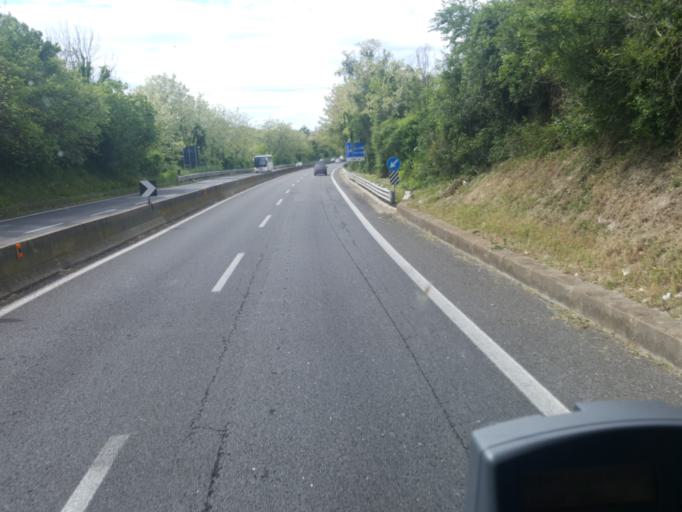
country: IT
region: Latium
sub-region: Citta metropolitana di Roma Capitale
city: Ponte Galeria-La Pisana
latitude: 41.8893
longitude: 12.3013
